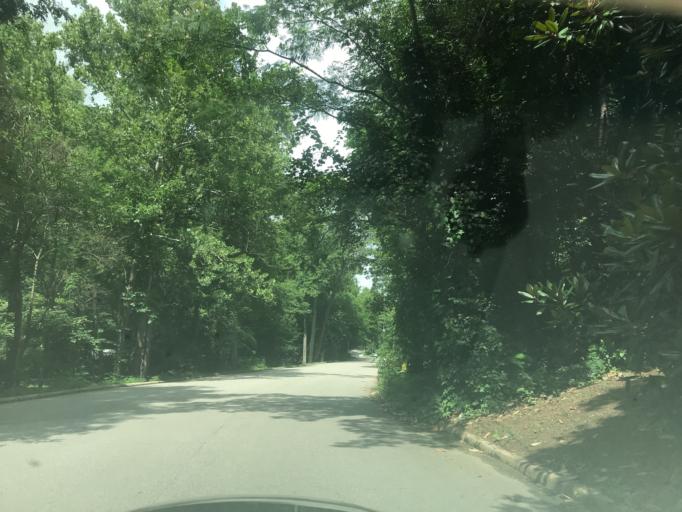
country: US
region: North Carolina
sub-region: Wake County
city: West Raleigh
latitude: 35.8125
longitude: -78.6395
